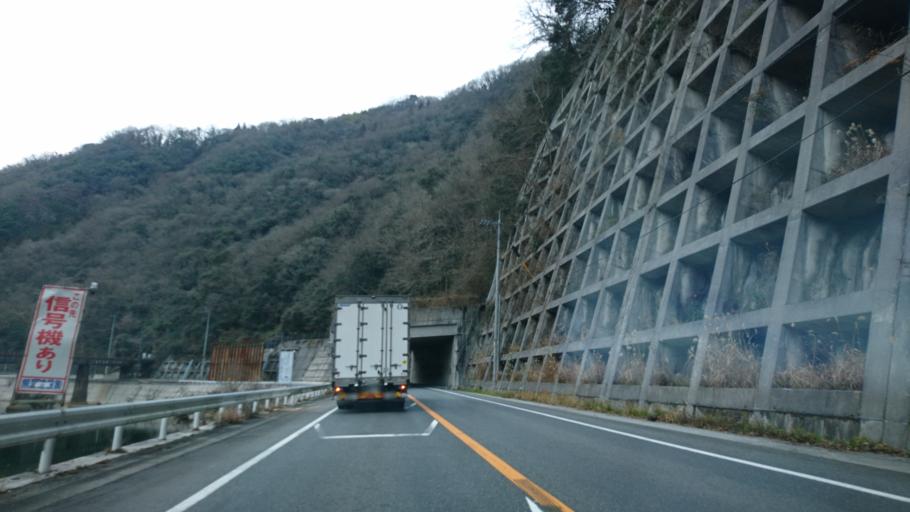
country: JP
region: Okayama
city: Niimi
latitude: 34.9125
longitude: 133.5315
